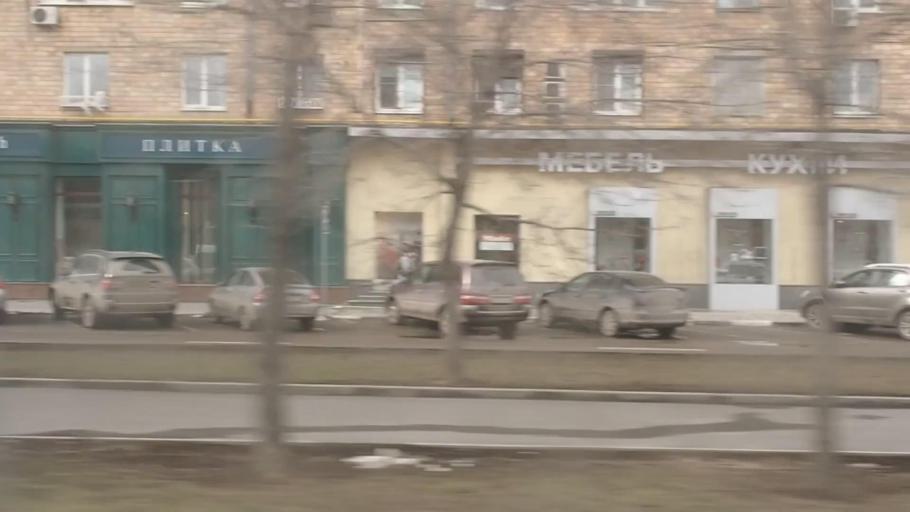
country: RU
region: Moskovskaya
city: Leninskiye Gory
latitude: 55.6989
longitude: 37.5640
